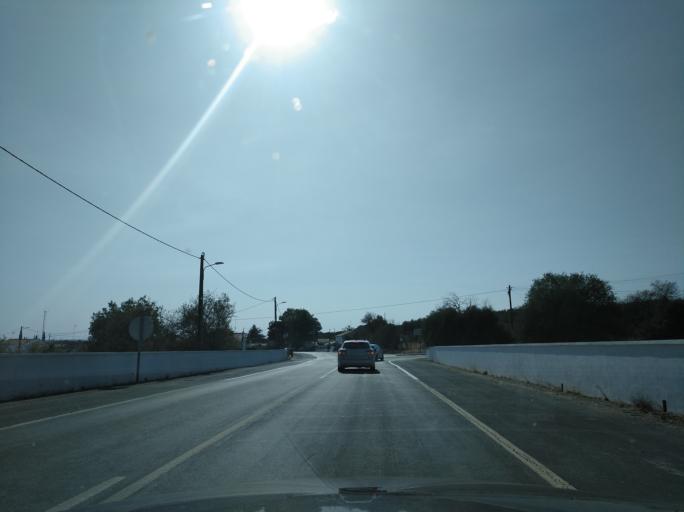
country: ES
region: Andalusia
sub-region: Provincia de Huelva
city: Rosal de la Frontera
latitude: 37.9496
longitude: -7.3022
